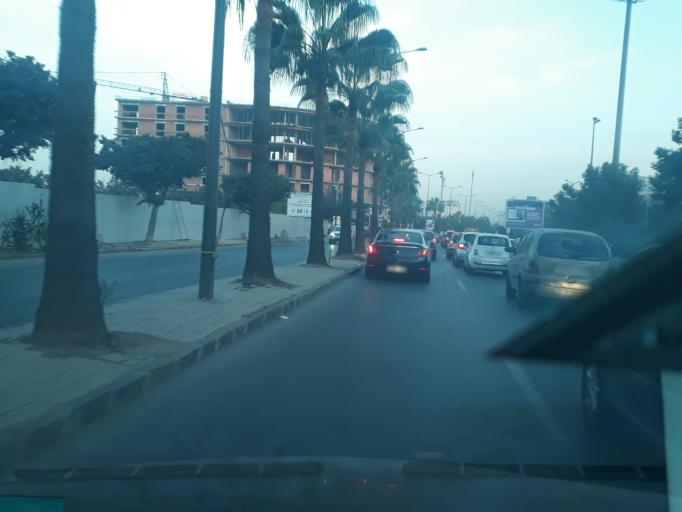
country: MA
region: Grand Casablanca
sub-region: Casablanca
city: Casablanca
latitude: 33.5799
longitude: -7.6468
